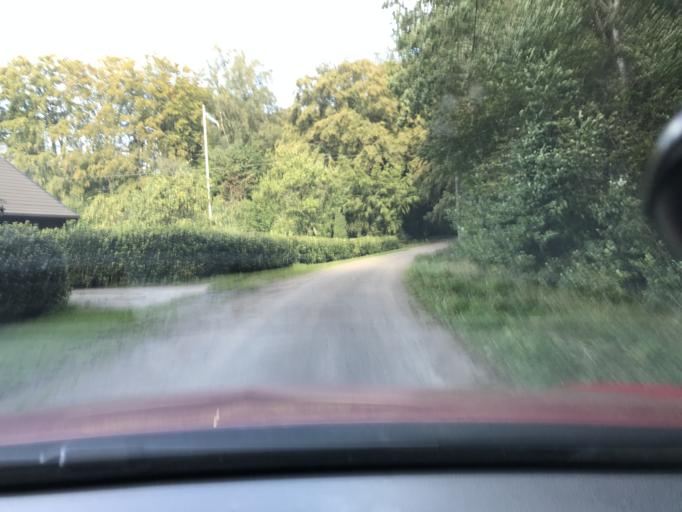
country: SE
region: Skane
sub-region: Hassleholms Kommun
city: Sosdala
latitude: 56.0036
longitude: 13.7044
